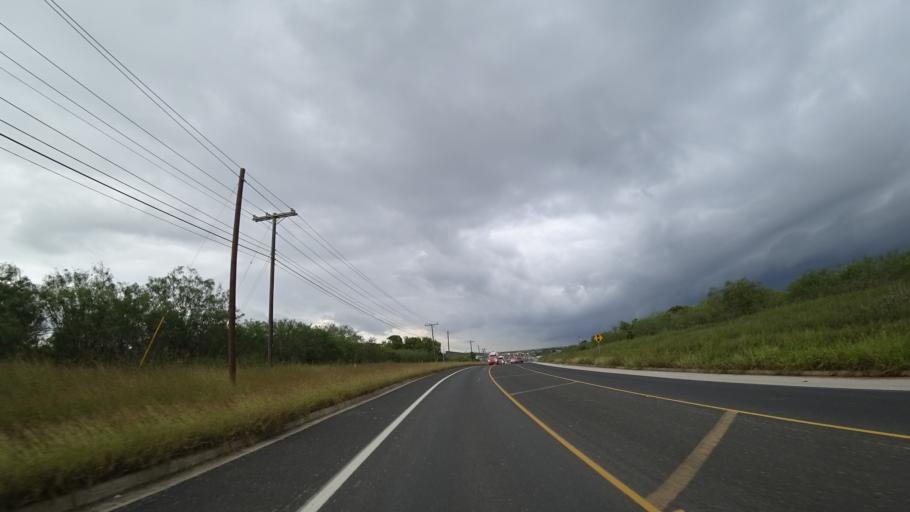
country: US
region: Texas
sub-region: Travis County
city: Onion Creek
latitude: 30.1642
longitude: -97.7278
